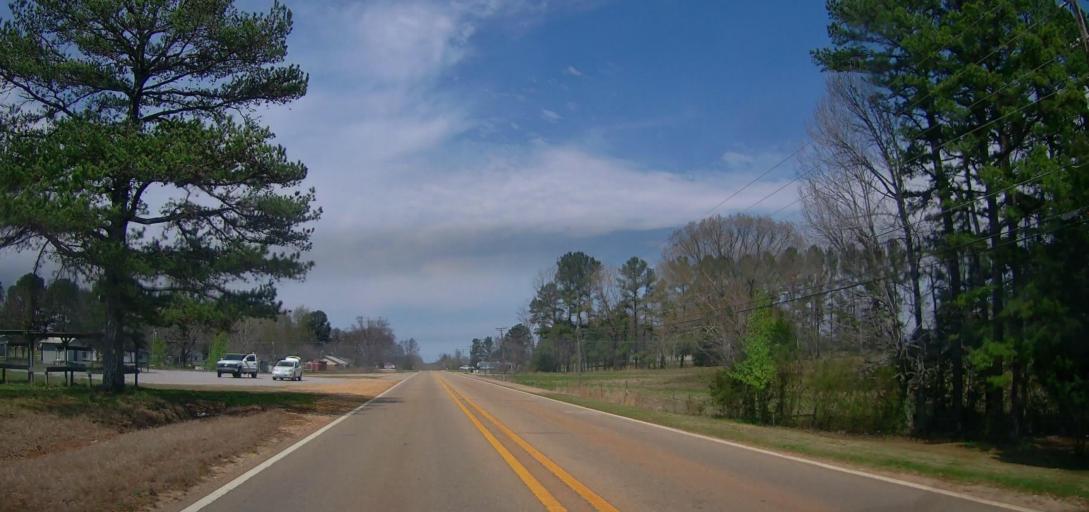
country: US
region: Mississippi
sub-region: Union County
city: New Albany
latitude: 34.4540
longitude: -88.9735
